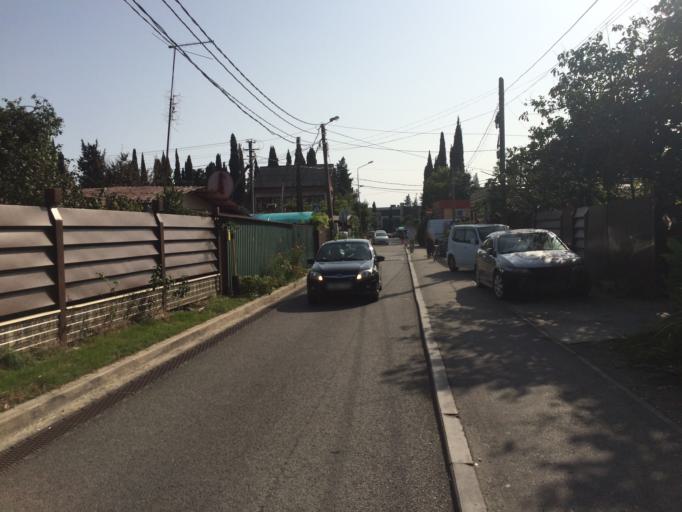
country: RU
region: Krasnodarskiy
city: Adler
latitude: 43.3936
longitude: 39.9818
